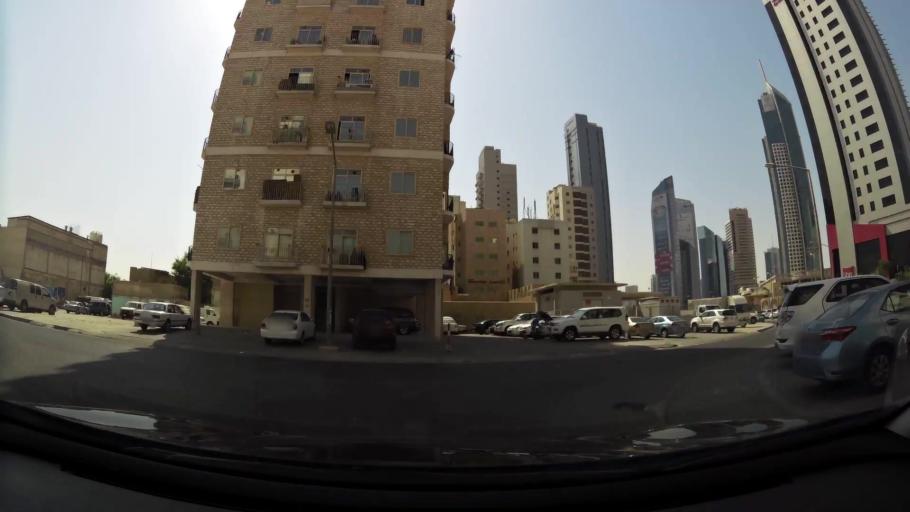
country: KW
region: Al Asimah
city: Ad Dasmah
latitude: 29.3785
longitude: 47.9950
